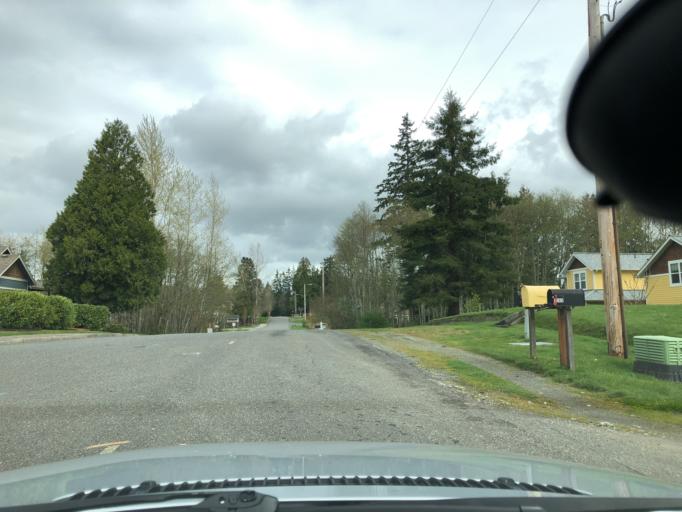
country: US
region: Washington
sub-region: Whatcom County
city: Blaine
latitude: 48.9767
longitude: -122.7353
